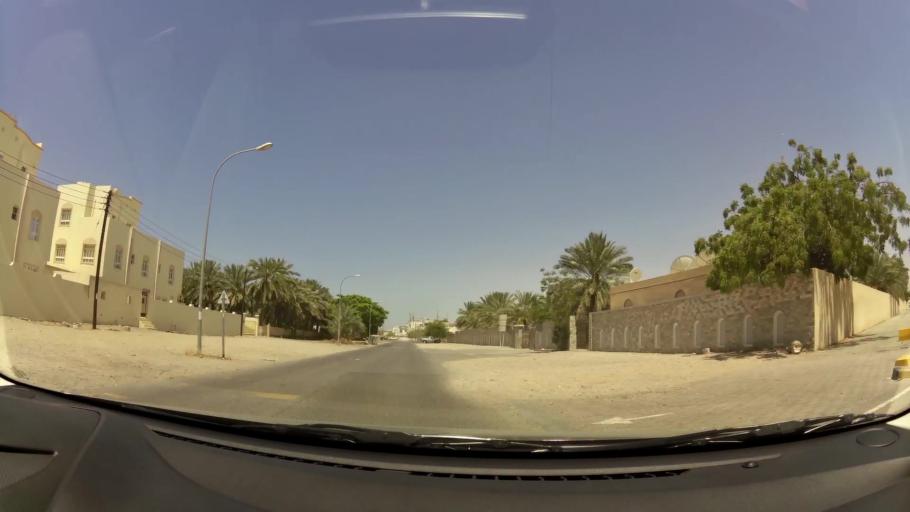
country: OM
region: Muhafazat Masqat
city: As Sib al Jadidah
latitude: 23.6178
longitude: 58.2303
